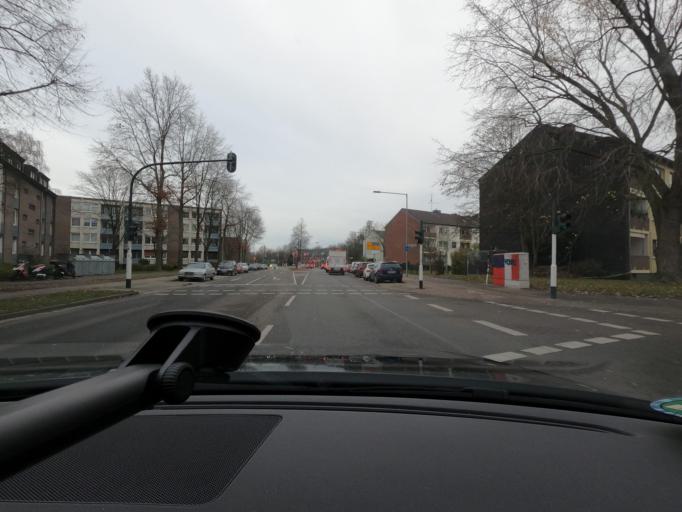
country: DE
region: North Rhine-Westphalia
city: Tonisvorst
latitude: 51.3469
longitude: 6.5235
